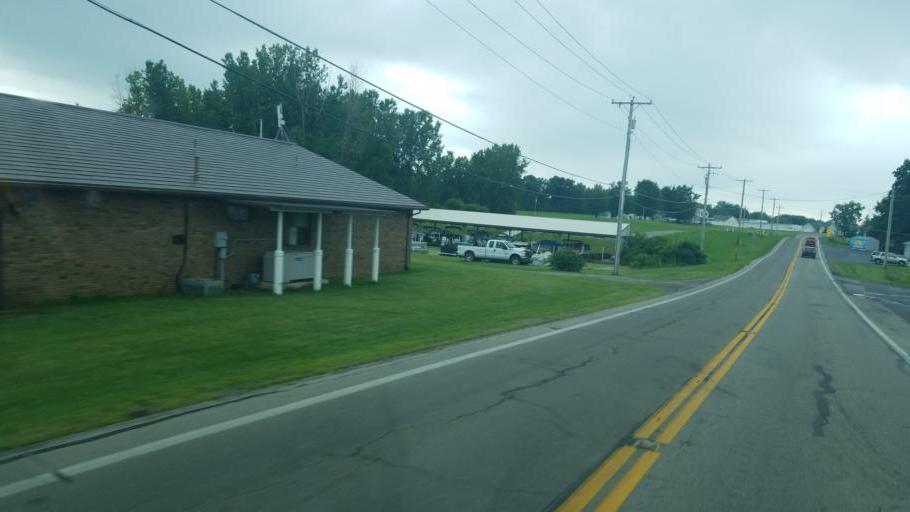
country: US
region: Ohio
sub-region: Logan County
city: Russells Point
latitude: 40.5274
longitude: -83.8555
